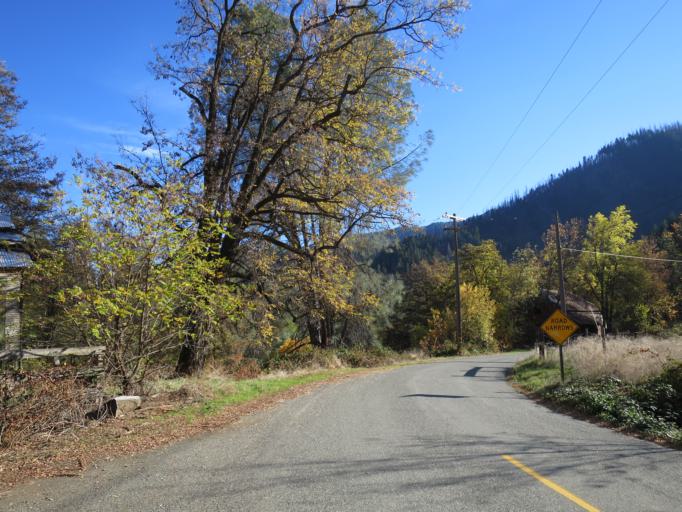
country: US
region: California
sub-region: Trinity County
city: Weaverville
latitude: 40.7733
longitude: -123.1286
